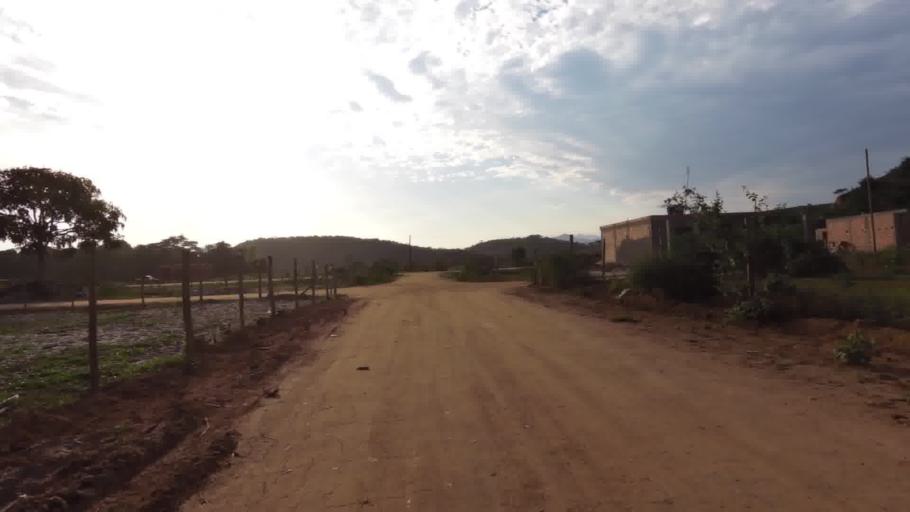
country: BR
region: Espirito Santo
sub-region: Piuma
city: Piuma
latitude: -20.8431
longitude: -40.7514
